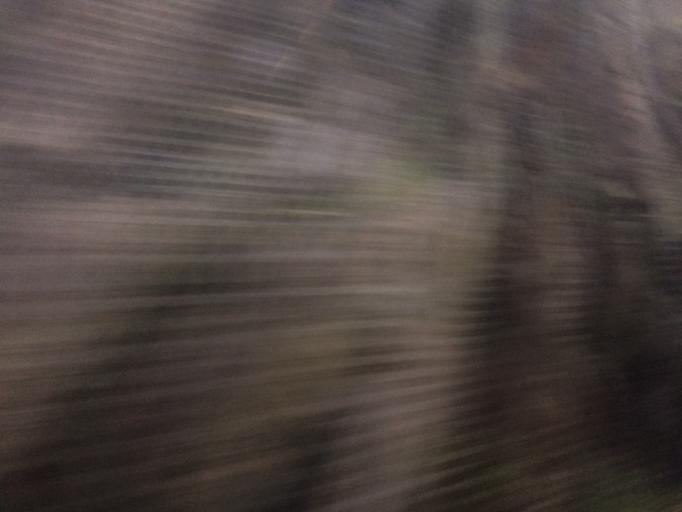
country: GB
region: Scotland
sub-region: North Lanarkshire
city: Kilsyth
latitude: 55.9635
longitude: -4.0259
